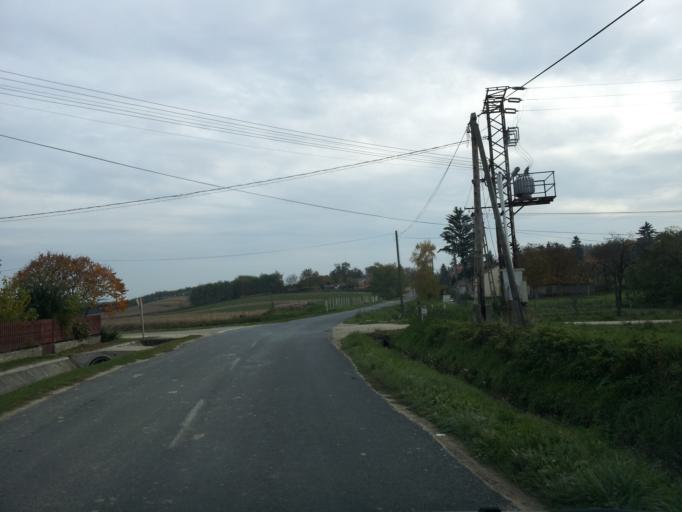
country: HU
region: Gyor-Moson-Sopron
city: Pannonhalma
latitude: 47.4743
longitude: 17.7072
